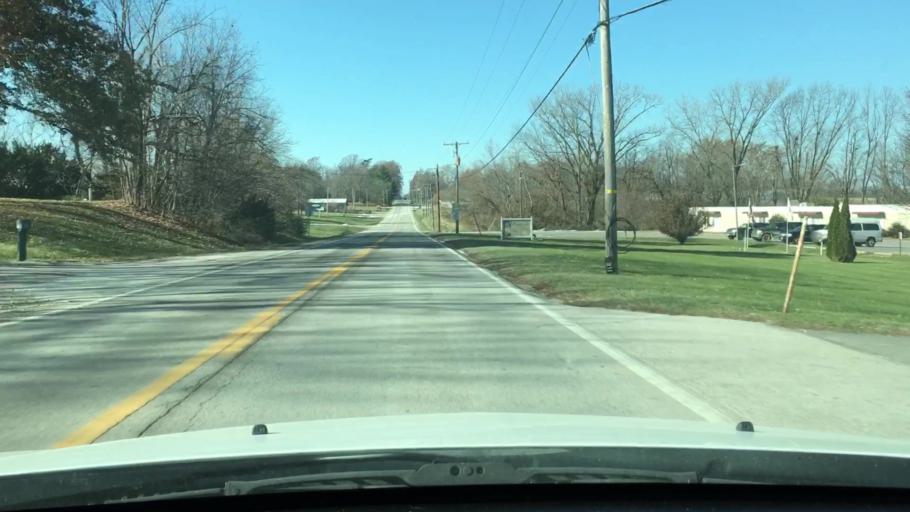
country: US
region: Illinois
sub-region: Pike County
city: Pittsfield
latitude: 39.6067
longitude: -90.7855
